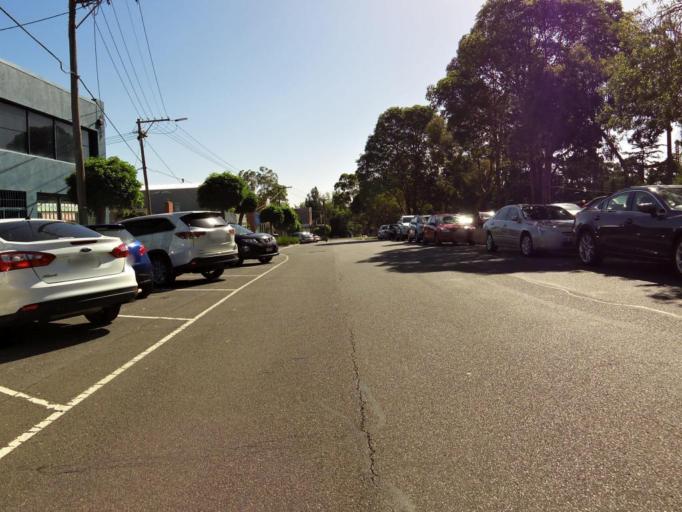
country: AU
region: Victoria
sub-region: Monash
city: Ashwood
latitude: -37.8744
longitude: 145.1133
